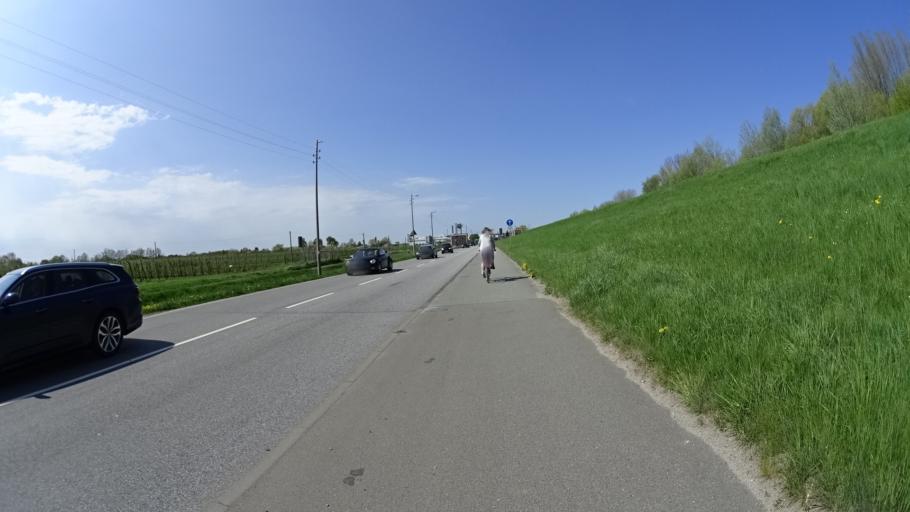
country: DE
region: Lower Saxony
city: Neu Wulmstorf
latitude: 53.5294
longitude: 9.8093
